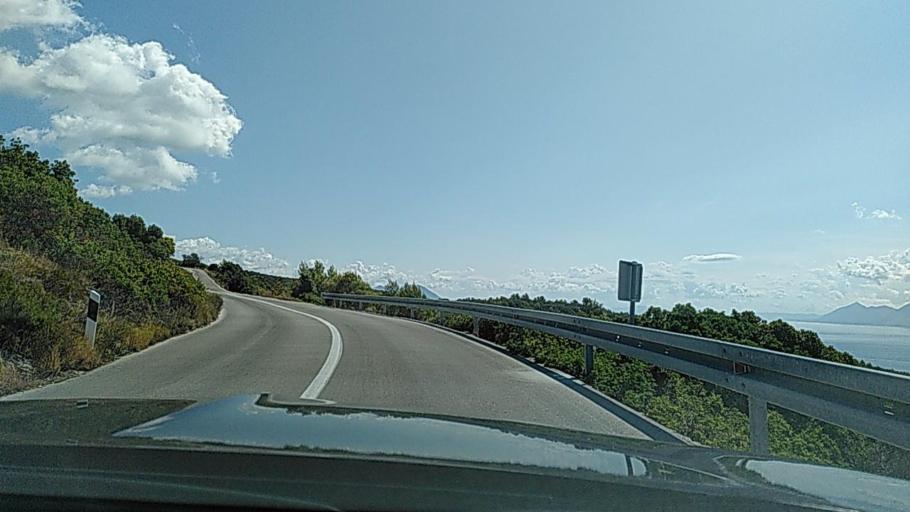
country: HR
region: Dubrovacko-Neretvanska
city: Orebic
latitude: 43.1222
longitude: 17.1114
